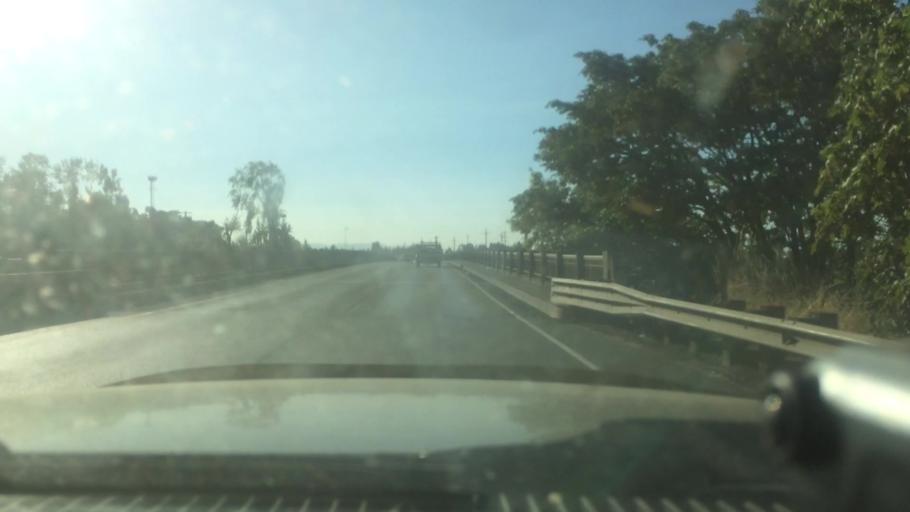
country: US
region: Oregon
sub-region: Lane County
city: Eugene
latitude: 44.0948
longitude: -123.1057
